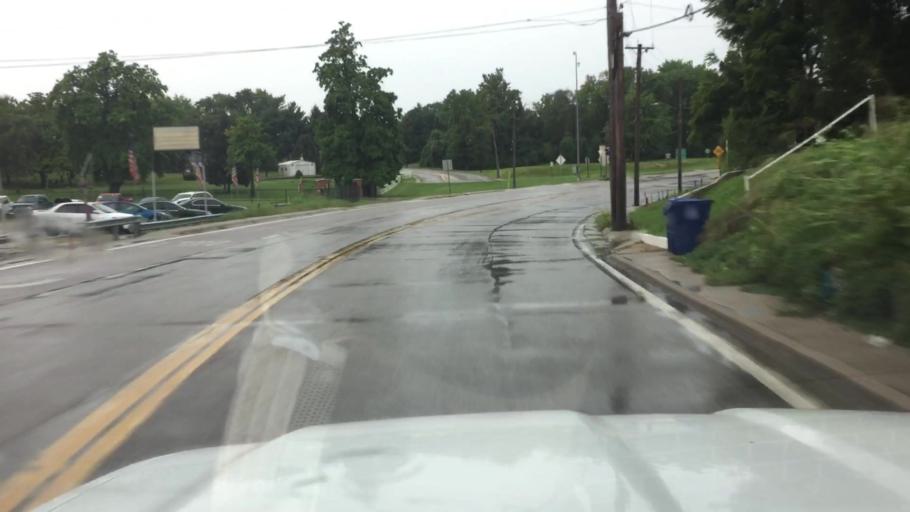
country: US
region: Missouri
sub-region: Saint Louis County
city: Lemay
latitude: 38.5234
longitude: -90.2774
